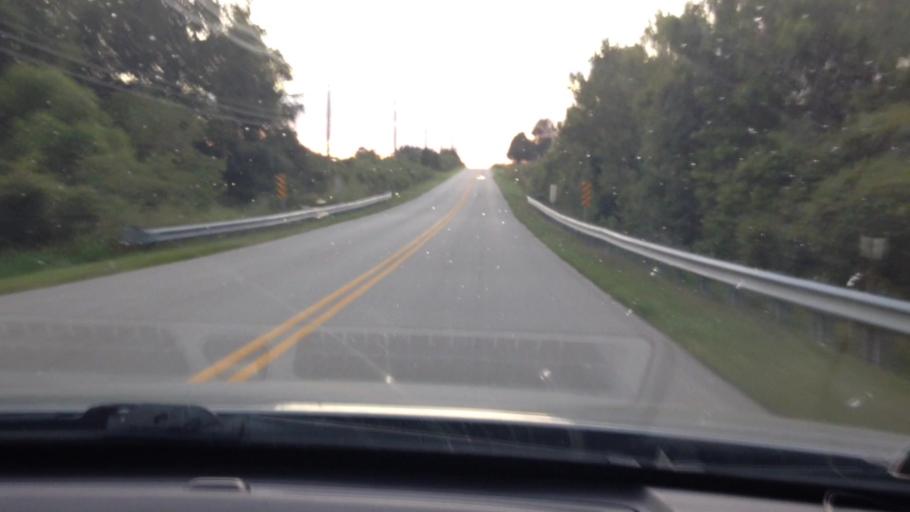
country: US
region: Kansas
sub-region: Leavenworth County
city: Lansing
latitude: 39.1868
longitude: -94.8544
